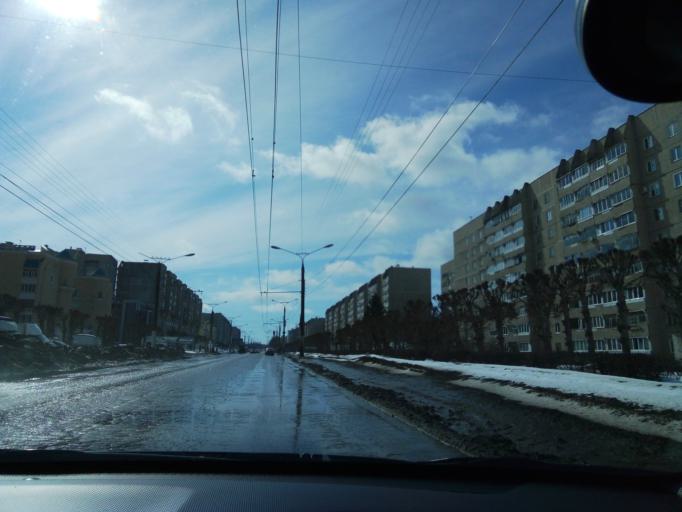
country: RU
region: Chuvashia
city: Novyye Lapsary
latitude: 56.1175
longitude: 47.1929
